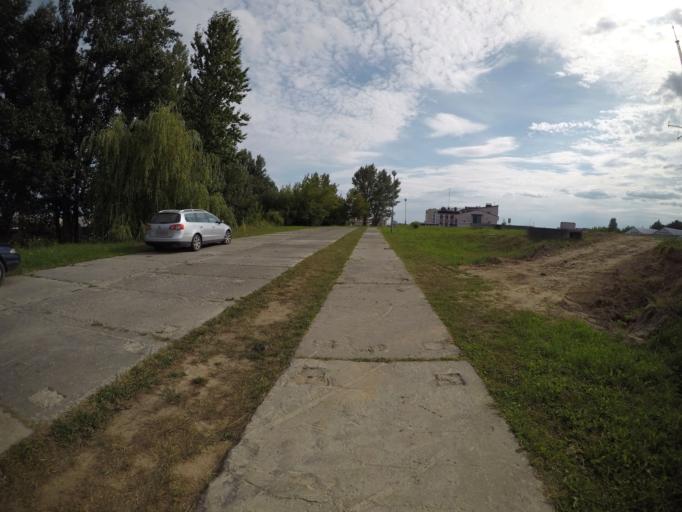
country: BY
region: Grodnenskaya
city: Hrodna
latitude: 53.7030
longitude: 23.8277
